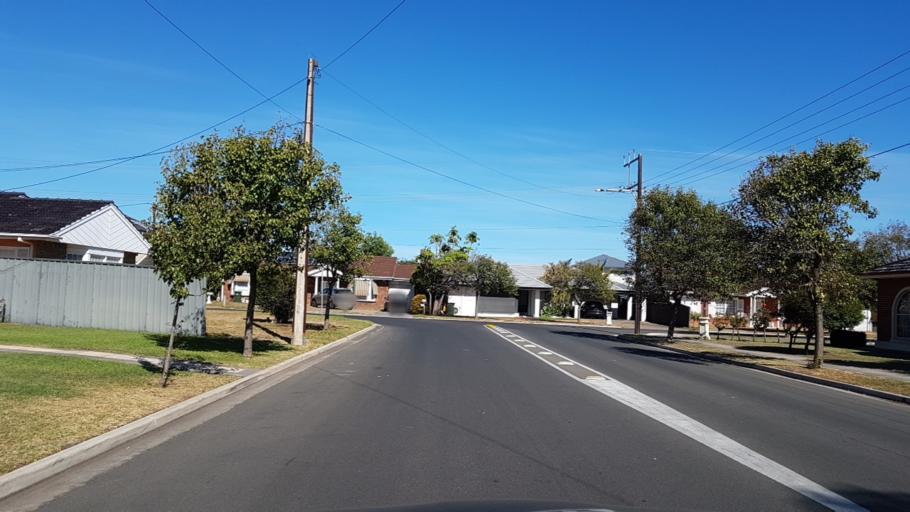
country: AU
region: South Australia
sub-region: Charles Sturt
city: Henley Beach
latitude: -34.9398
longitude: 138.5088
